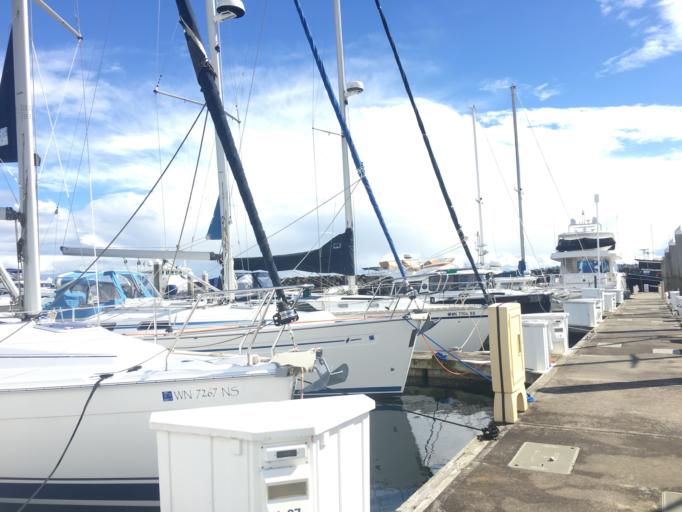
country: US
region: Washington
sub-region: King County
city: Seattle
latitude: 47.6284
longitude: -122.3888
